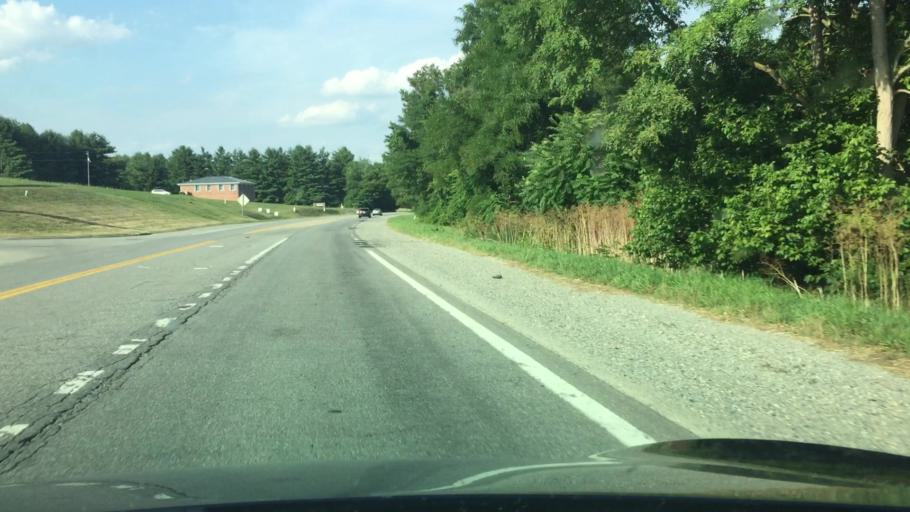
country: US
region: Virginia
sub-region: Pulaski County
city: Dublin
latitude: 37.1155
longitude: -80.6693
